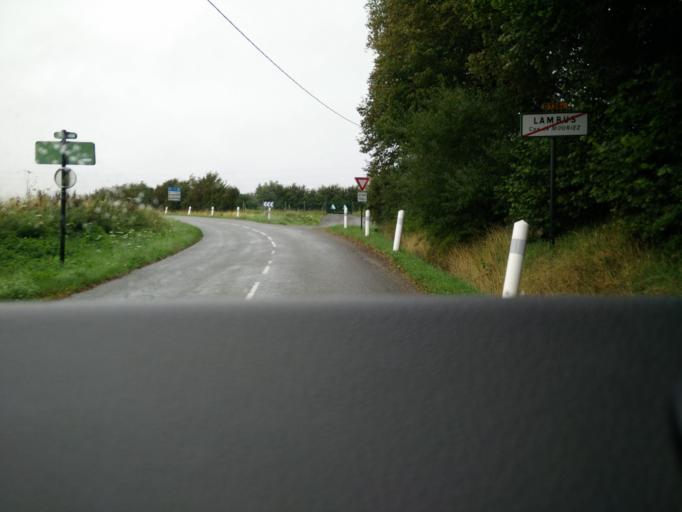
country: FR
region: Nord-Pas-de-Calais
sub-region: Departement du Pas-de-Calais
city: Marconnelle
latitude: 50.3677
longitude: 1.9520
